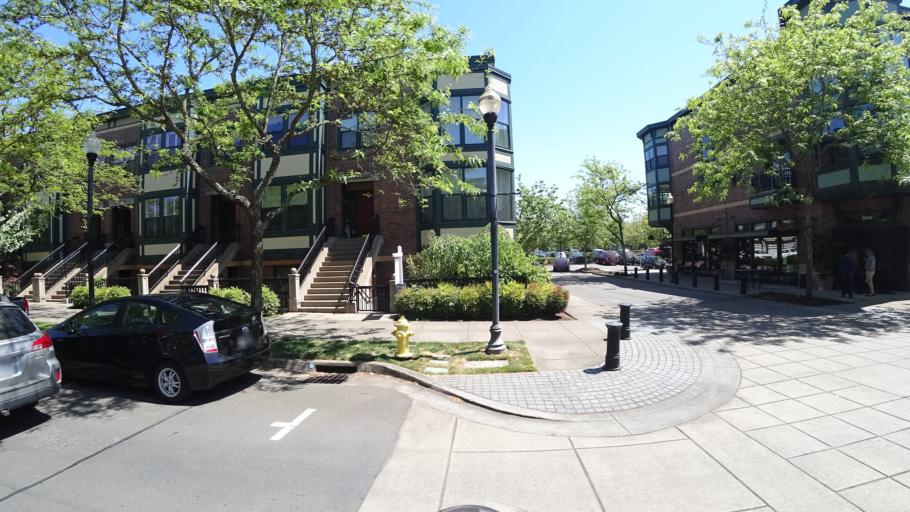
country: US
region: Oregon
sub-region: Washington County
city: Rockcreek
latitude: 45.5349
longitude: -122.9169
